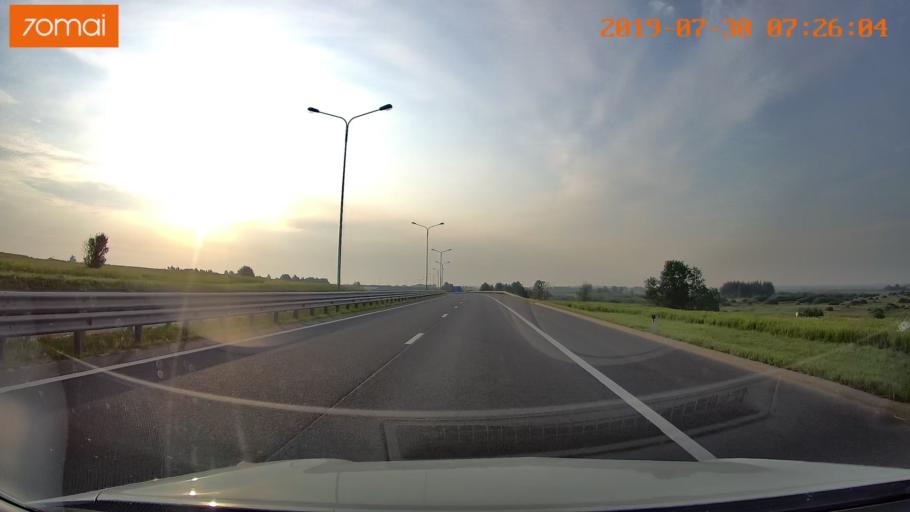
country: RU
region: Kaliningrad
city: Gvardeysk
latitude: 54.6839
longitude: 20.8509
